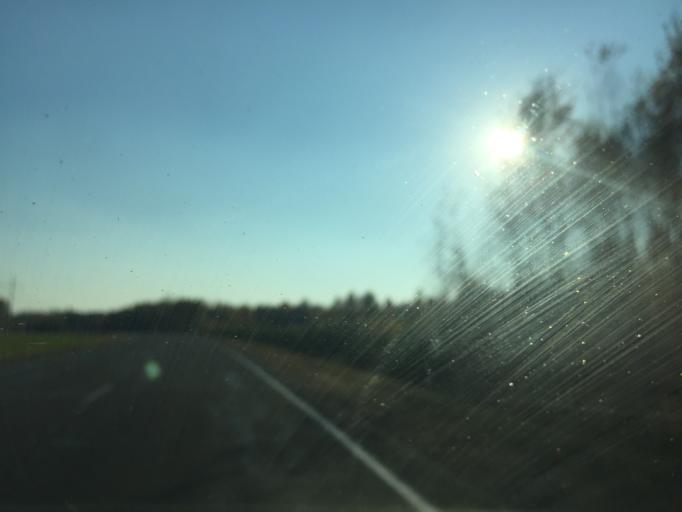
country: BY
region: Gomel
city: Dobrush
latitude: 52.3529
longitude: 31.2299
